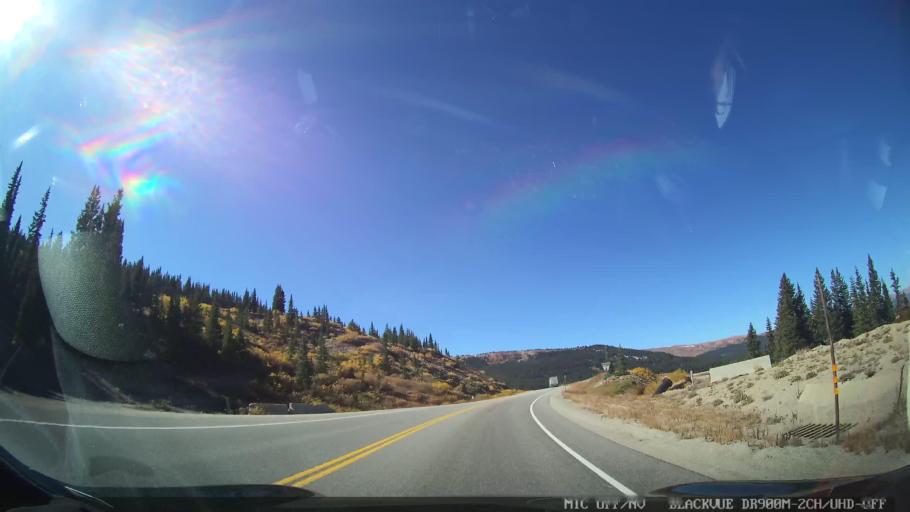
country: US
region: Colorado
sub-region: Summit County
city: Breckenridge
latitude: 39.3924
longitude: -106.1877
